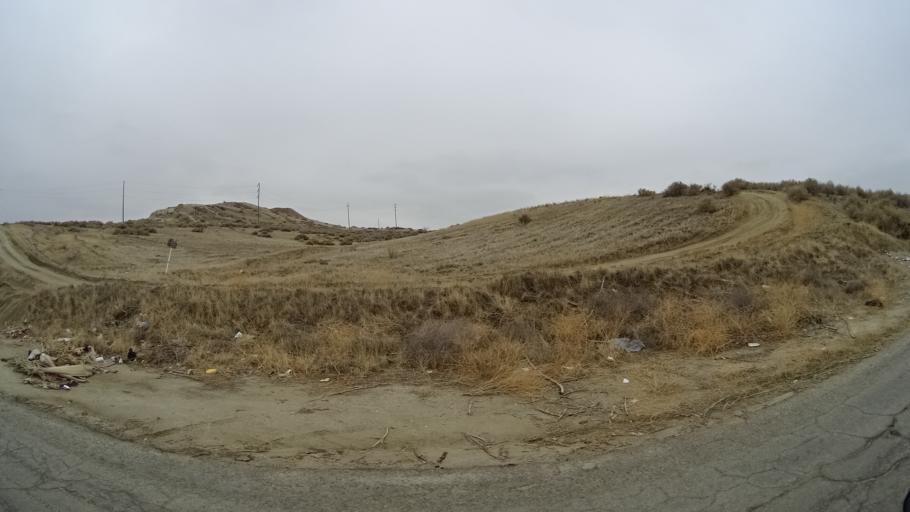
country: US
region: California
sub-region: Kern County
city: Oildale
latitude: 35.4231
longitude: -118.9374
